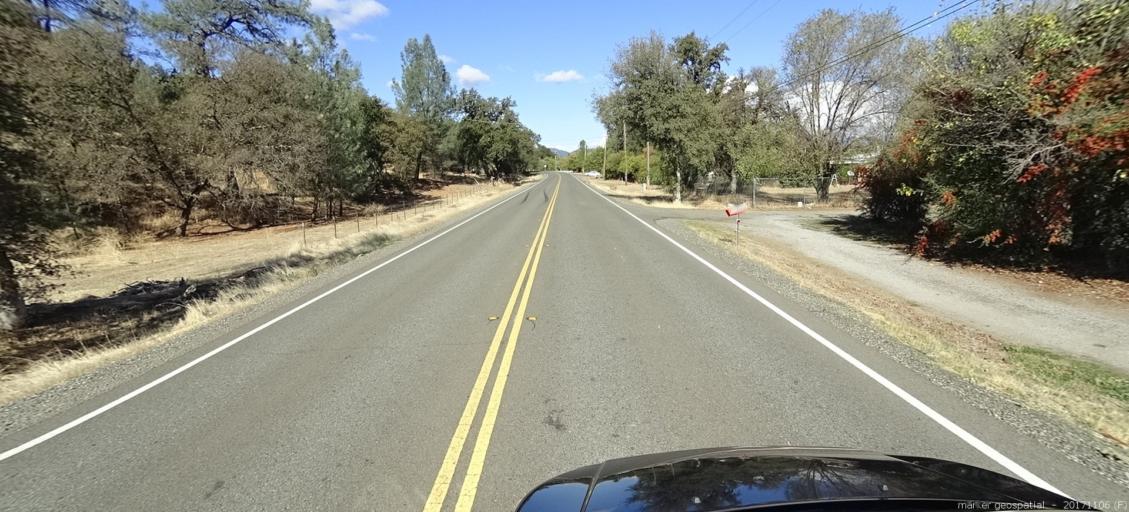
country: US
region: California
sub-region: Shasta County
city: Bella Vista
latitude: 40.6293
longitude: -122.2358
